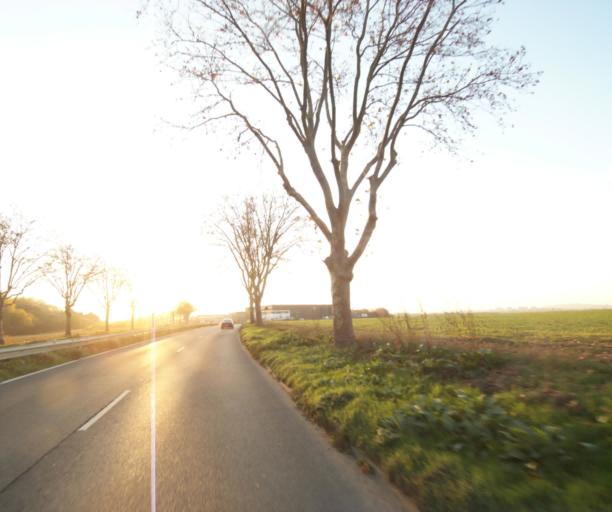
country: FR
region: Ile-de-France
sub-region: Departement du Val-d'Oise
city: Gonesse
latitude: 48.9960
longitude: 2.4608
